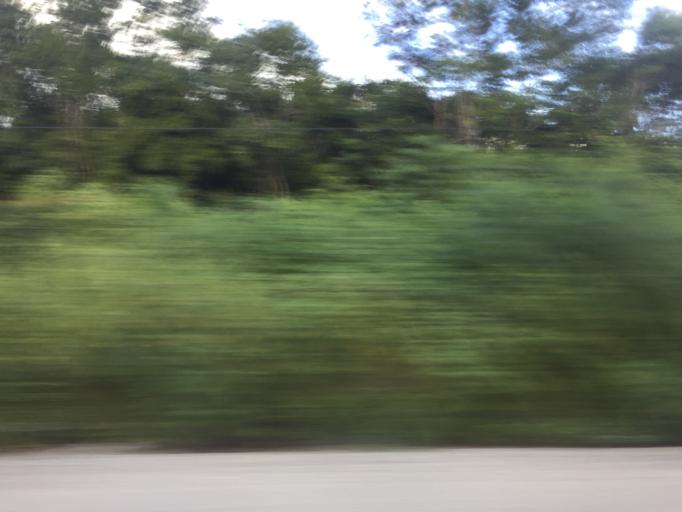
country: MX
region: Quintana Roo
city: Tulum
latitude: 20.2768
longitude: -87.4882
